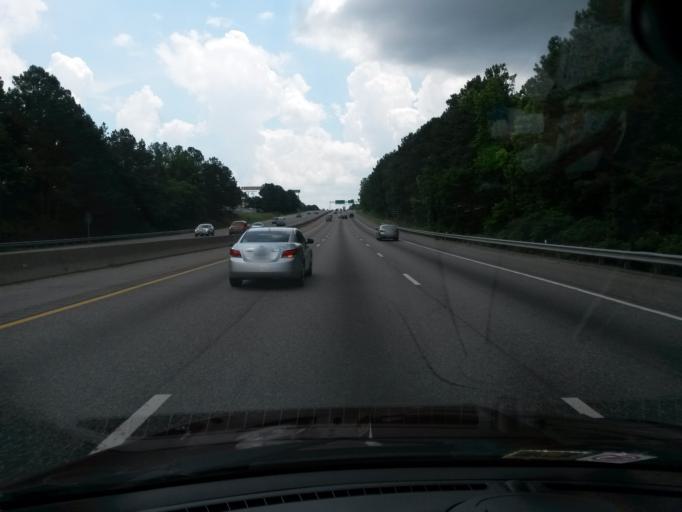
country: US
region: Virginia
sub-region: Chesterfield County
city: Bellwood
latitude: 37.4080
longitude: -77.4260
